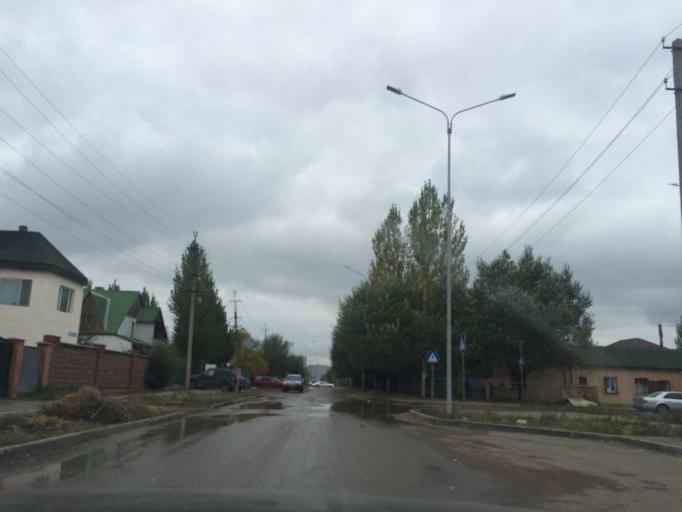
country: KZ
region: Astana Qalasy
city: Astana
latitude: 51.1378
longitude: 71.5033
